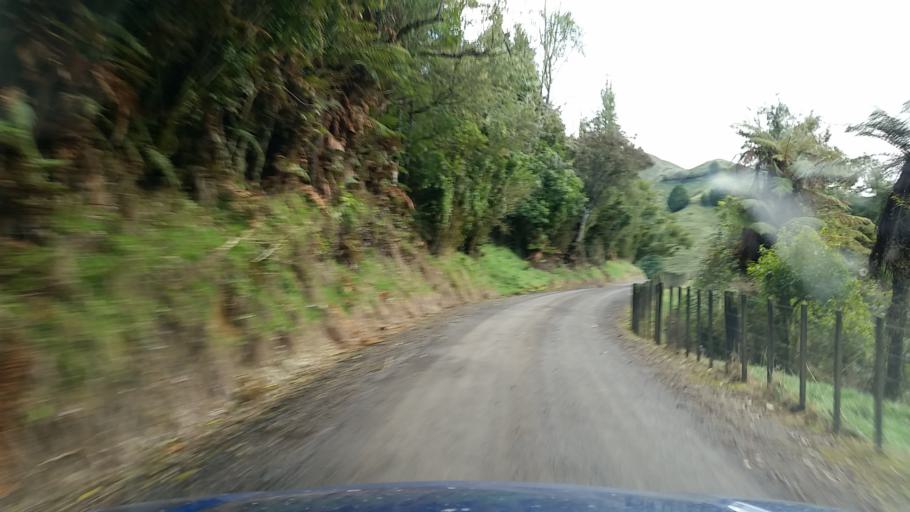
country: NZ
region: Taranaki
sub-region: New Plymouth District
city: Waitara
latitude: -39.0930
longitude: 174.8389
